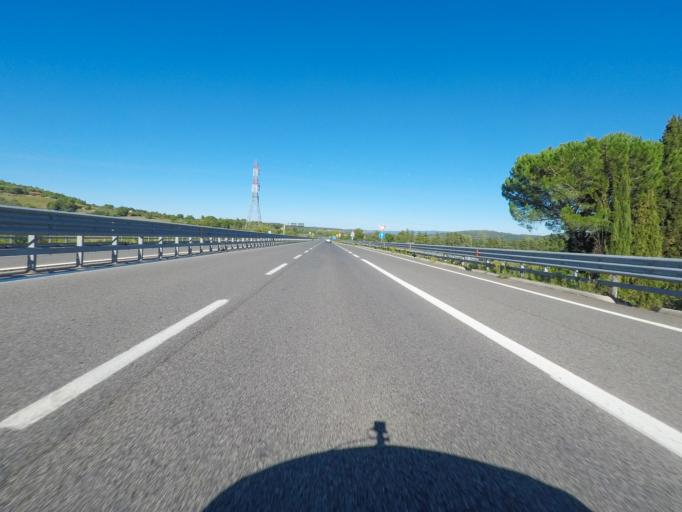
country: IT
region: Tuscany
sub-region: Provincia di Grosseto
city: Campagnatico
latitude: 42.9189
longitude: 11.2587
